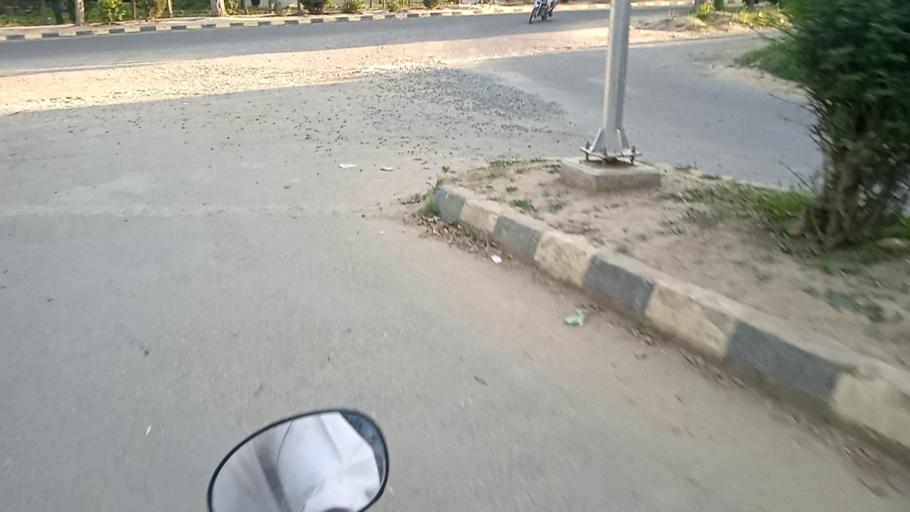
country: PK
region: Khyber Pakhtunkhwa
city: Mingora
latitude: 34.8300
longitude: 72.3426
